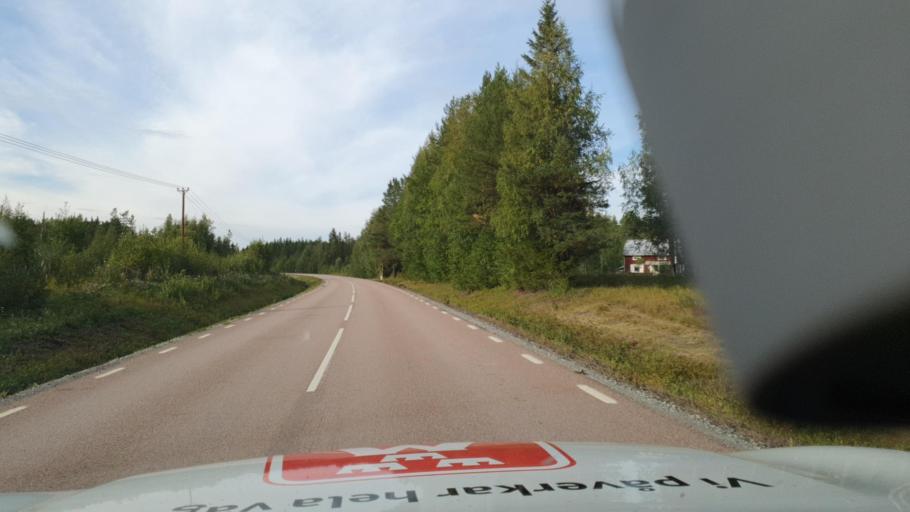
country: SE
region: Jaemtland
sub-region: Stroemsunds Kommun
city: Stroemsund
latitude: 63.7826
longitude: 15.7159
